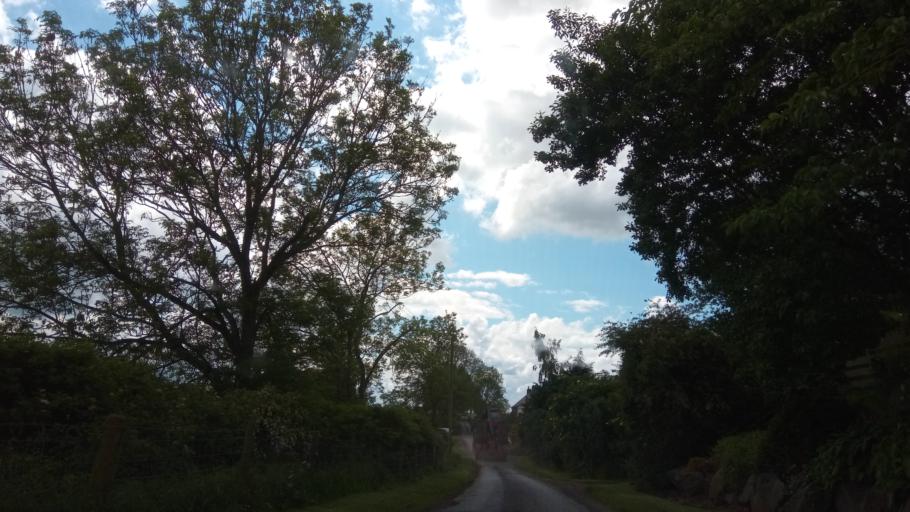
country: GB
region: Scotland
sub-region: The Scottish Borders
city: Coldstream
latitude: 55.5733
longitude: -2.3243
